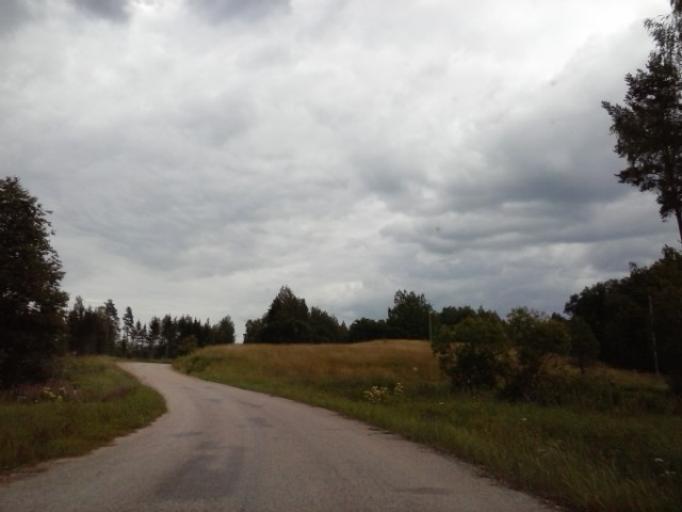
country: EE
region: Vorumaa
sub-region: Voru linn
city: Voru
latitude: 57.7452
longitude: 27.1207
